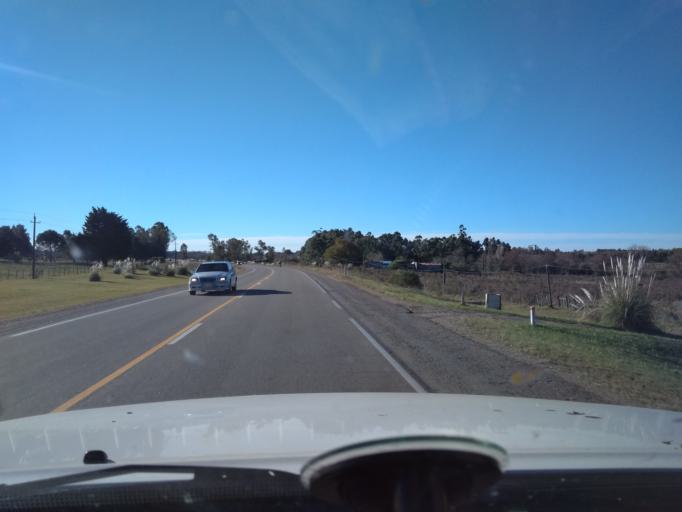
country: UY
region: Canelones
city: Sauce
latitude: -34.6101
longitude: -56.0484
